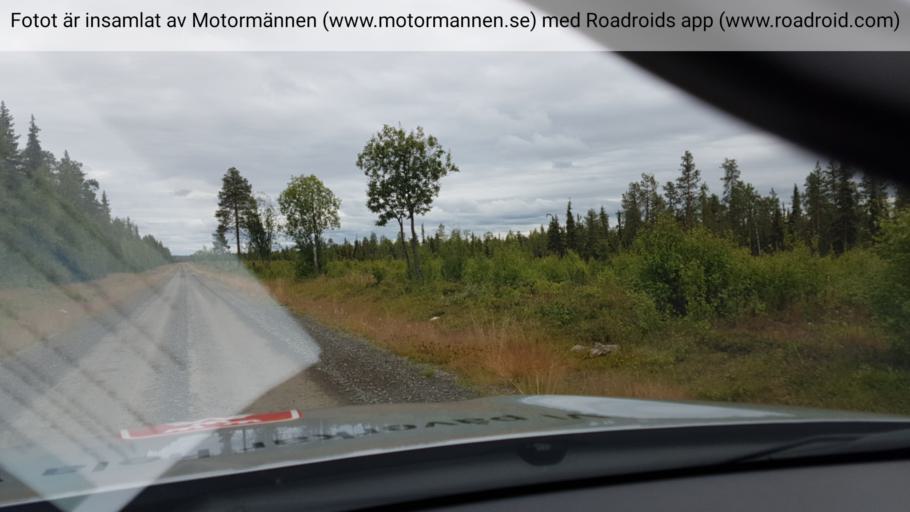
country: SE
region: Norrbotten
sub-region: Pajala Kommun
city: Pajala
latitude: 67.0766
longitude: 22.7888
